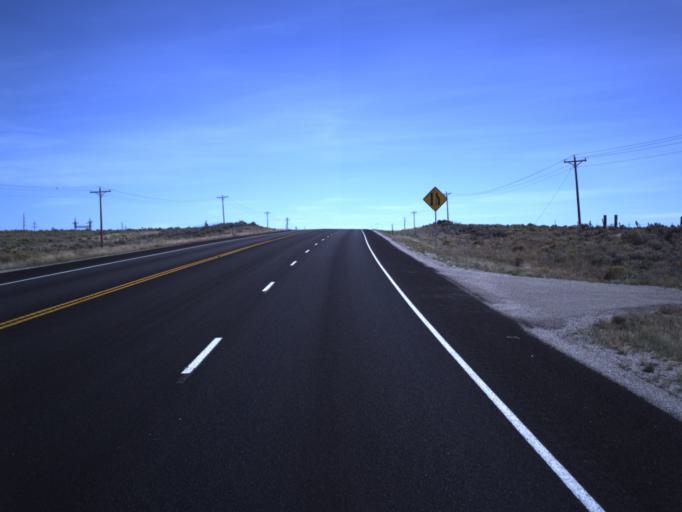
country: US
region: Utah
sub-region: San Juan County
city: Monticello
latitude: 37.8723
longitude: -109.2615
